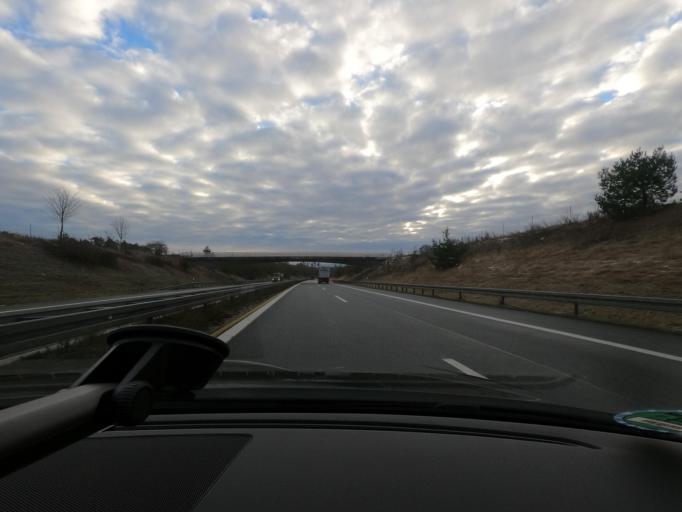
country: DE
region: Bavaria
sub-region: Upper Franconia
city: Lautertal
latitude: 50.3206
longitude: 10.9525
